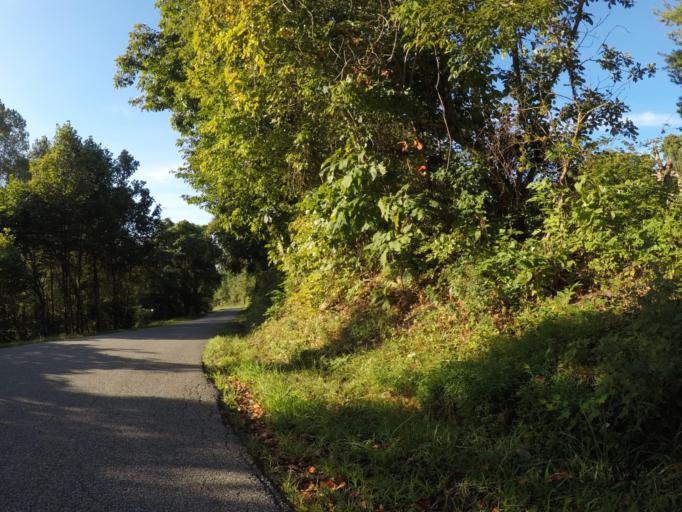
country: US
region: Ohio
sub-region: Lawrence County
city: Coal Grove
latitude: 38.5972
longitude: -82.5468
